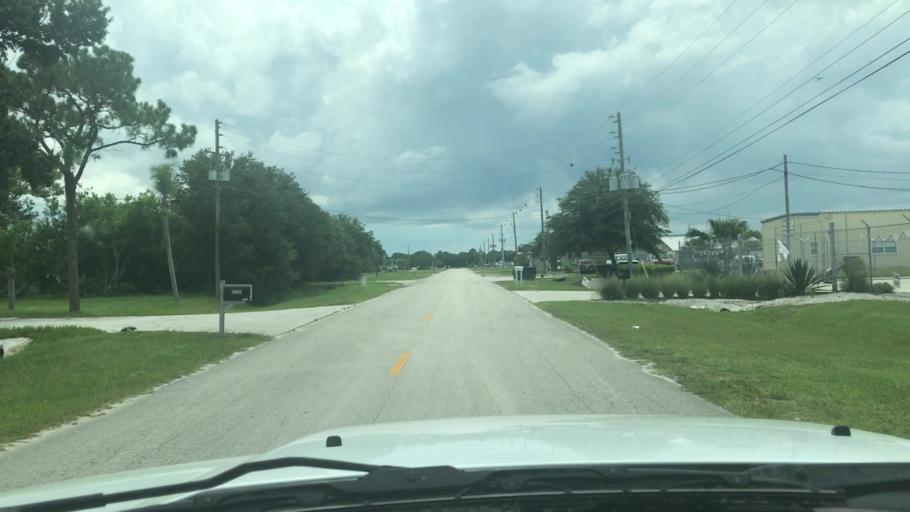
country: US
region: Florida
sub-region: Saint Lucie County
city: Fort Pierce North
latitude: 27.4937
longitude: -80.3522
